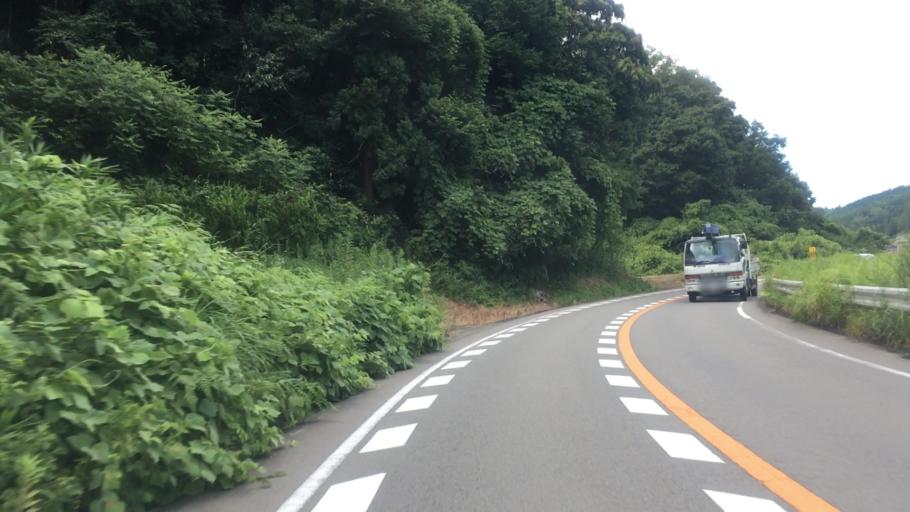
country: JP
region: Hyogo
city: Toyooka
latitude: 35.5342
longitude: 134.7884
